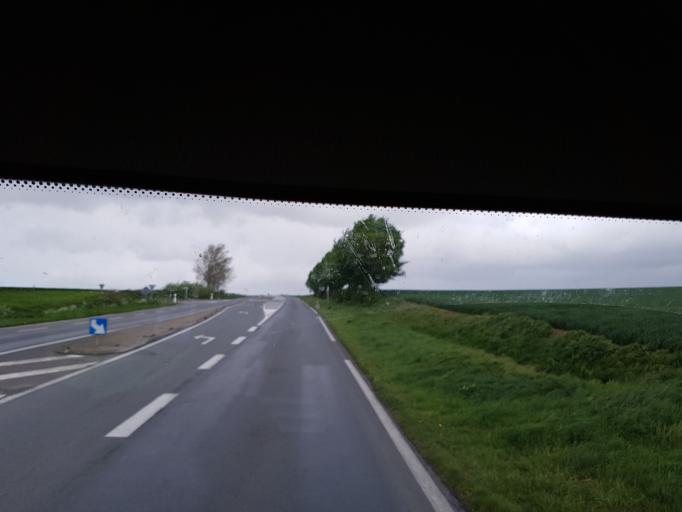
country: FR
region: Nord-Pas-de-Calais
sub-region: Departement du Nord
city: Raillencourt-Sainte-Olle
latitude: 50.2153
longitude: 3.1820
